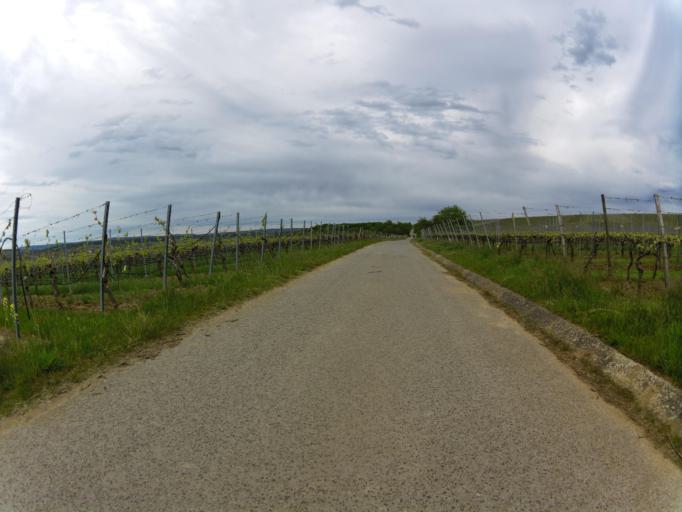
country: DE
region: Bavaria
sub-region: Regierungsbezirk Unterfranken
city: Nordheim
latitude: 49.8542
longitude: 10.1986
